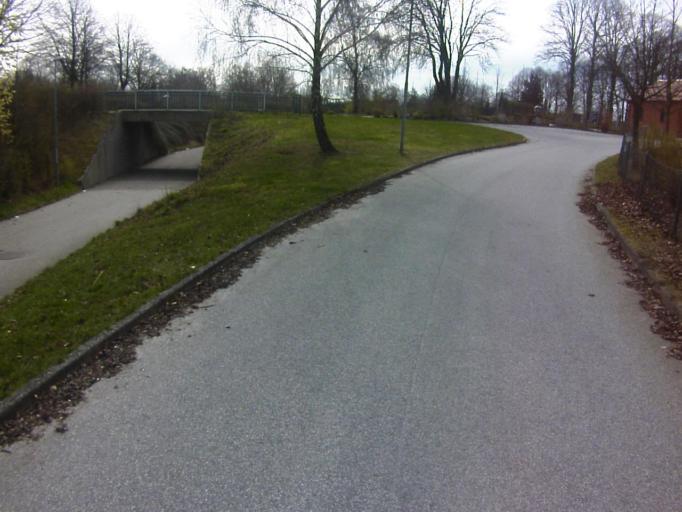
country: SE
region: Skane
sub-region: Kavlinge Kommun
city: Kaevlinge
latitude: 55.7935
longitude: 13.1058
